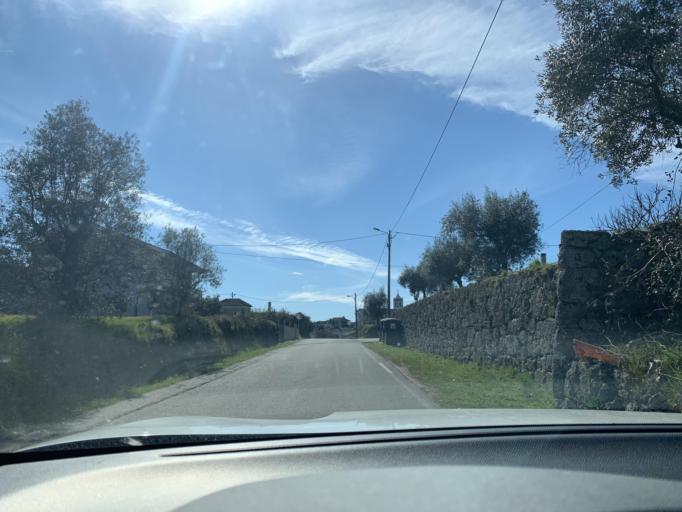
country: PT
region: Viseu
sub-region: Concelho de Tondela
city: Tondela
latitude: 40.5915
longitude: -8.0252
